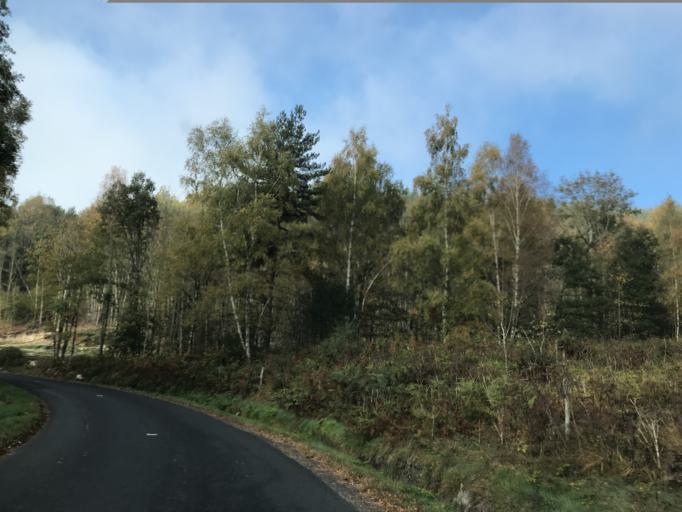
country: FR
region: Auvergne
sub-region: Departement du Puy-de-Dome
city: Celles-sur-Durolle
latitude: 45.7875
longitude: 3.6511
